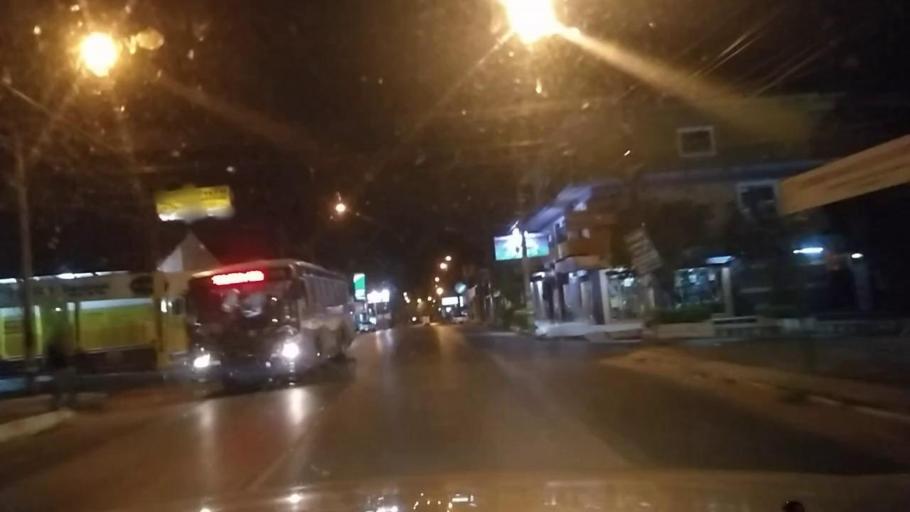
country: PY
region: Central
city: Ita
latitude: -25.5073
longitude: -57.3596
